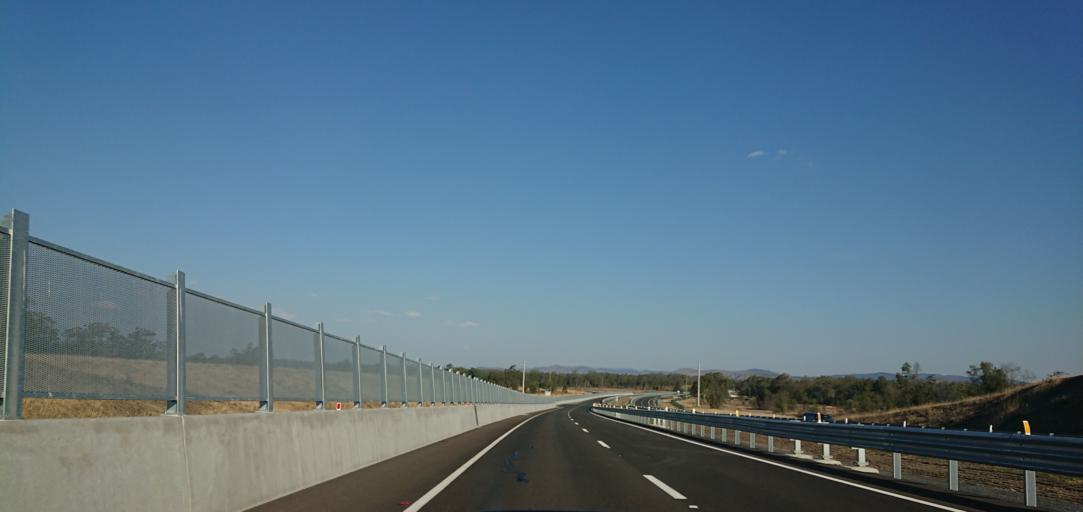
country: AU
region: Queensland
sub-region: Toowoomba
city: East Toowoomba
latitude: -27.5276
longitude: 152.0705
